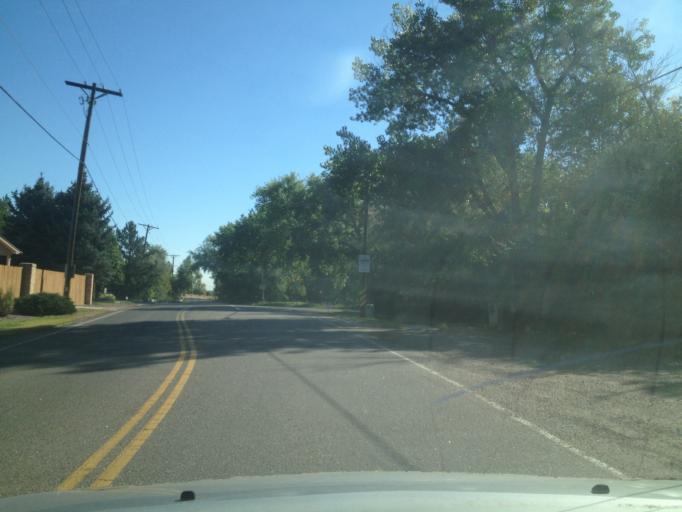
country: US
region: Colorado
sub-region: Jefferson County
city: Applewood
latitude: 39.7610
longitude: -105.1711
